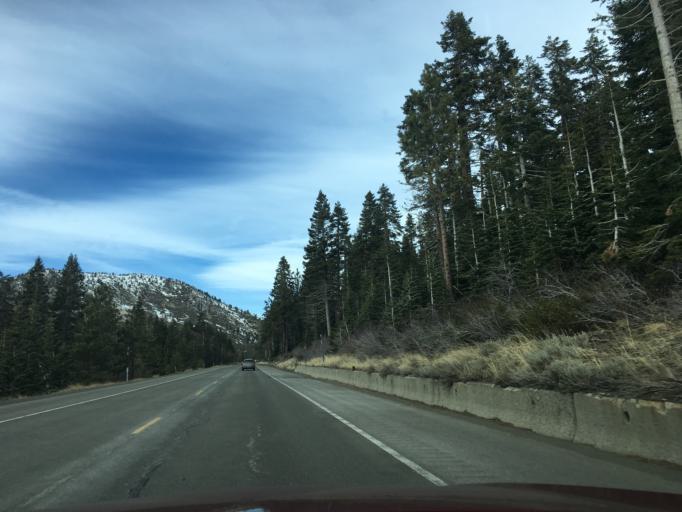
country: US
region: Nevada
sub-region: Washoe County
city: Incline Village
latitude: 39.2739
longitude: -119.9333
